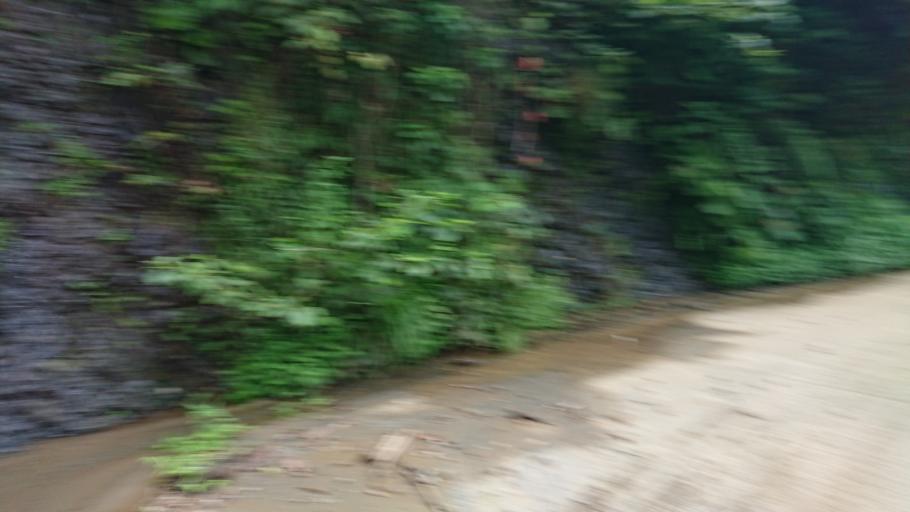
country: TR
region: Rize
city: Rize
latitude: 40.9886
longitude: 40.5120
